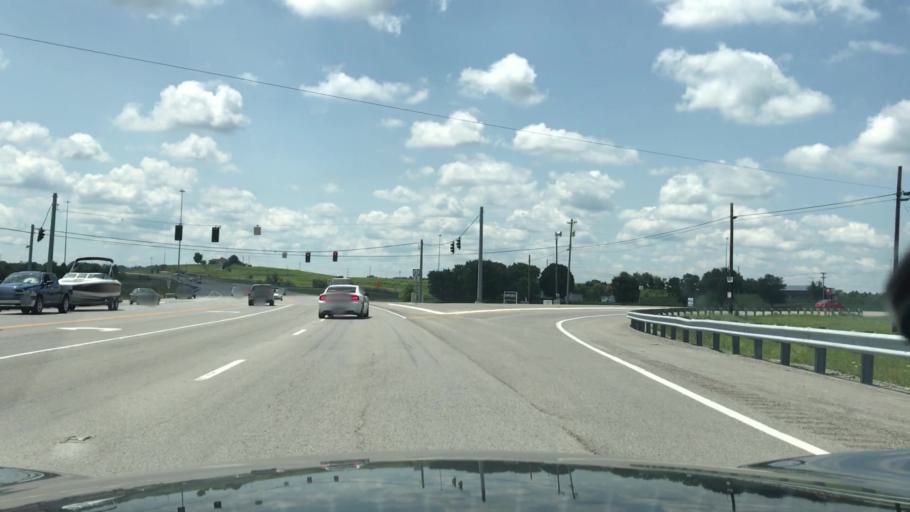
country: US
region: Kentucky
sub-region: Adair County
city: Columbia
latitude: 37.0767
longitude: -85.3379
